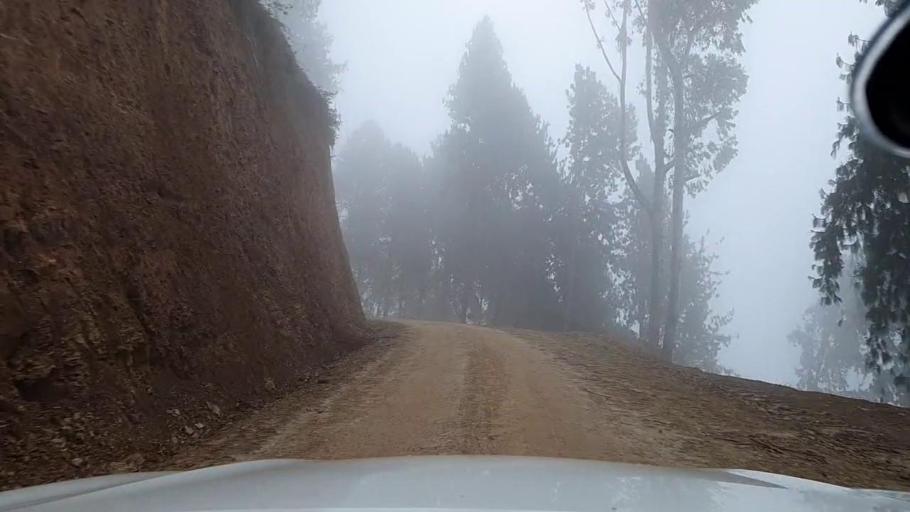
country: BI
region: Cibitoke
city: Cibitoke
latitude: -2.5957
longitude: 29.1946
